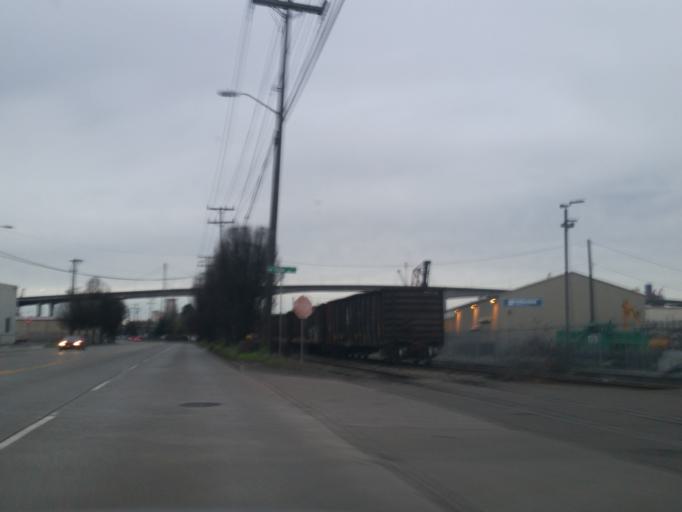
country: US
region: Washington
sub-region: King County
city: Seattle
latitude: 47.5652
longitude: -122.3529
